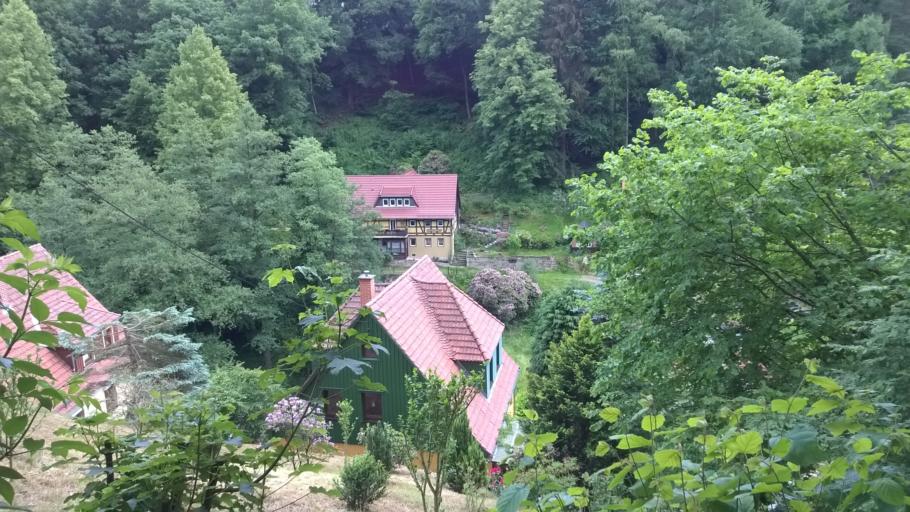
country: DE
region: Saxony
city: Hohnstein
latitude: 50.9604
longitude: 14.0814
